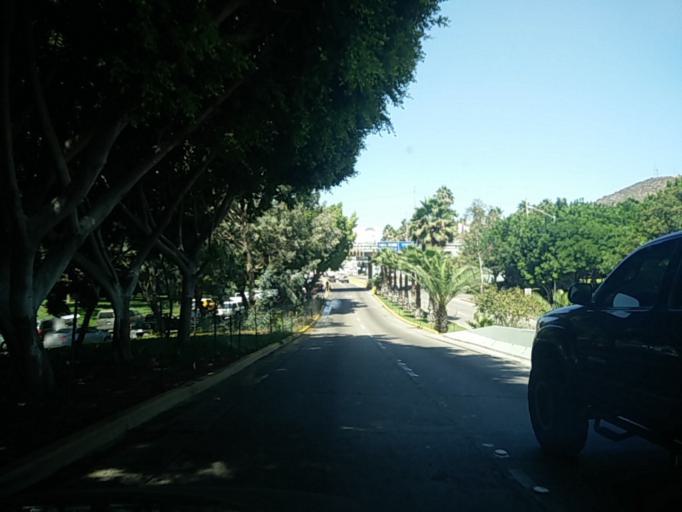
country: MX
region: Baja California
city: Tijuana
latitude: 32.5395
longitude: -117.0262
